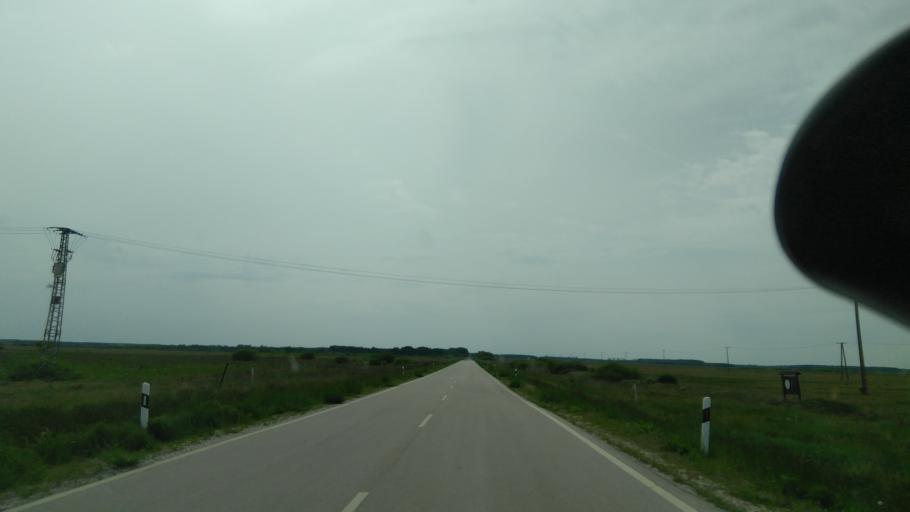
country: HU
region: Bekes
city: Mehkerek
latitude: 46.8673
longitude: 21.4916
